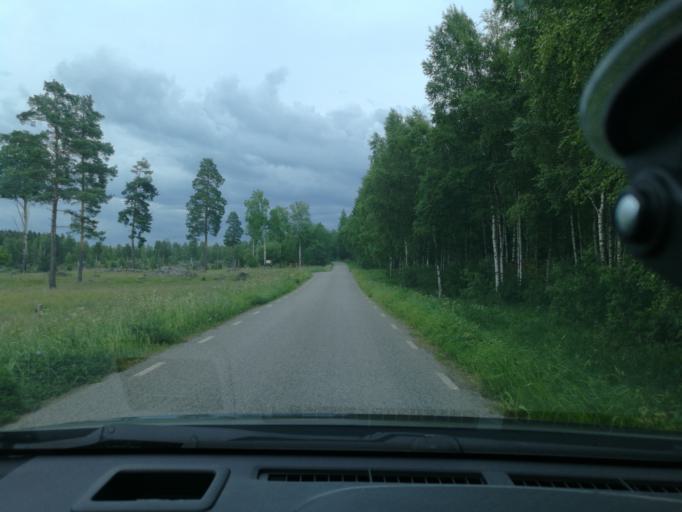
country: SE
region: Vaestmanland
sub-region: Vasteras
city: Skultuna
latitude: 59.8520
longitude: 16.3423
